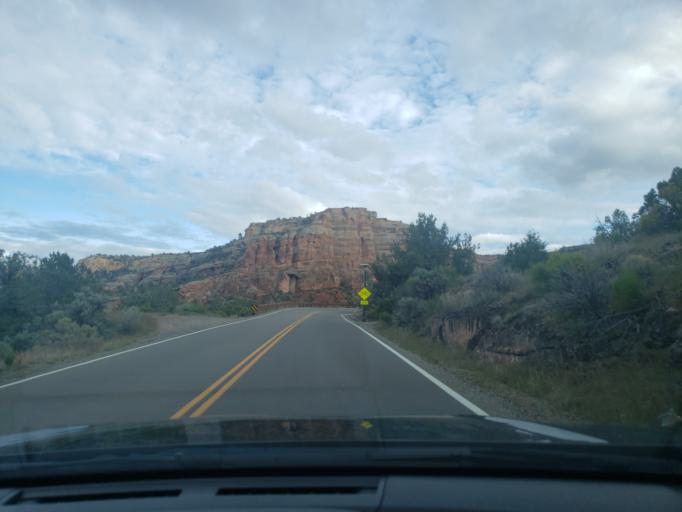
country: US
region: Colorado
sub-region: Mesa County
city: Redlands
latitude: 39.0281
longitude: -108.6359
